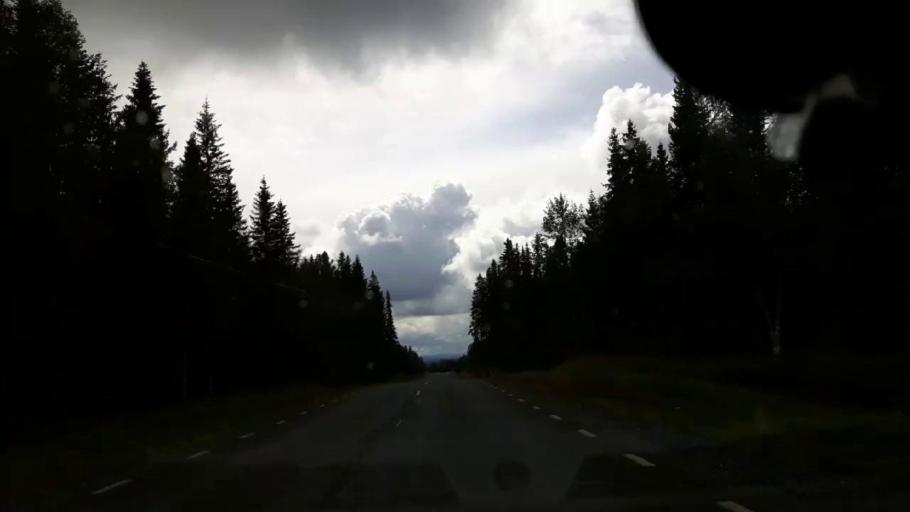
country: SE
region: Jaemtland
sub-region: Krokoms Kommun
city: Valla
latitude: 63.4302
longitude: 13.8043
